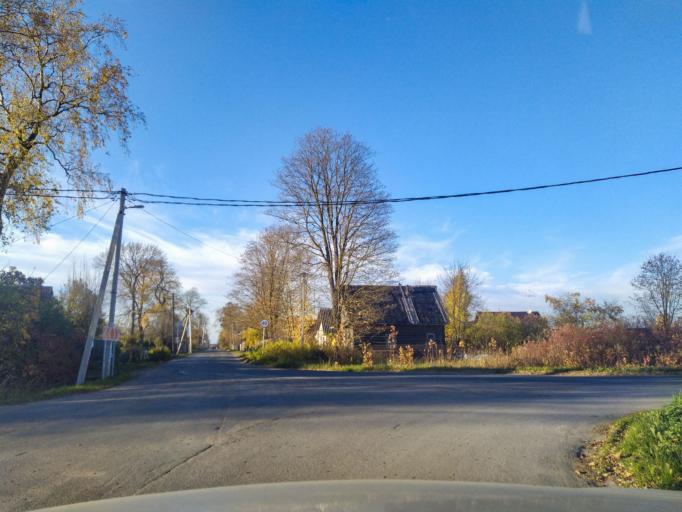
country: RU
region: Leningrad
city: Siverskiy
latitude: 59.3280
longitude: 30.0387
